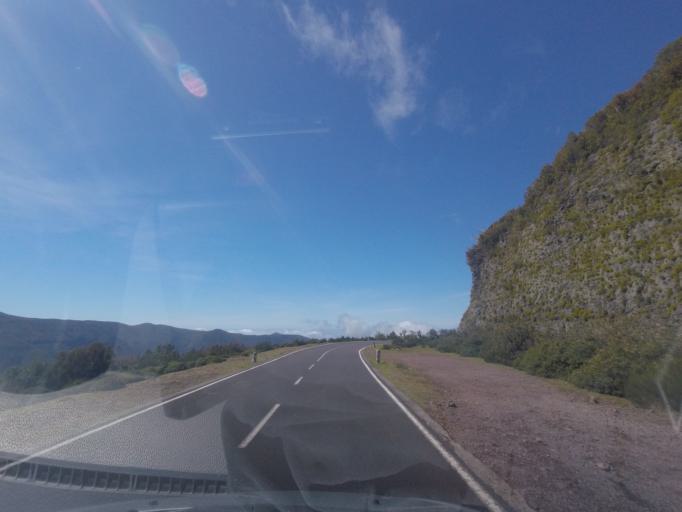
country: PT
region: Madeira
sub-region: Porto Moniz
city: Porto Moniz
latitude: 32.8024
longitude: -17.1390
